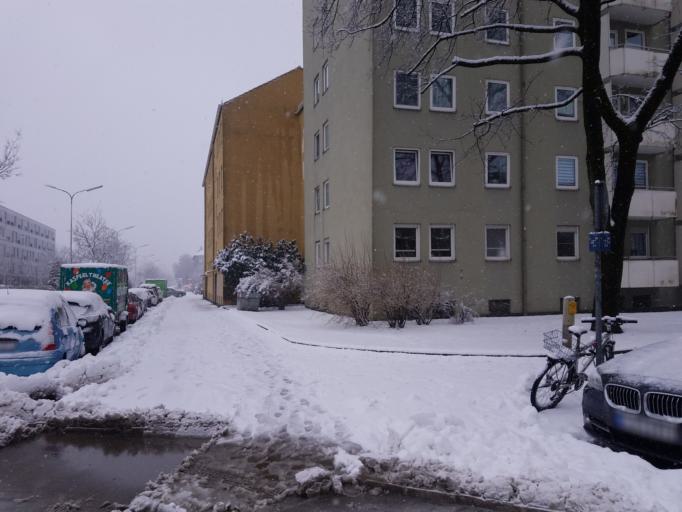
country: DE
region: Bavaria
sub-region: Upper Bavaria
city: Pasing
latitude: 48.1424
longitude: 11.5093
